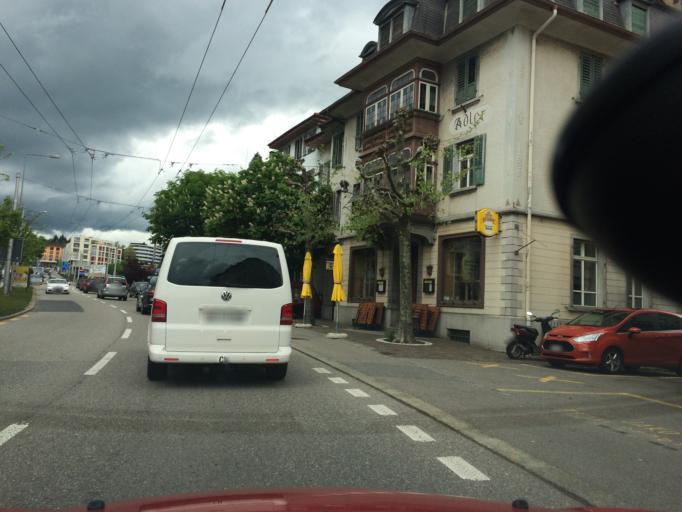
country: CH
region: Lucerne
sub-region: Hochdorf District
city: Emmen
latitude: 47.0780
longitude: 8.2757
